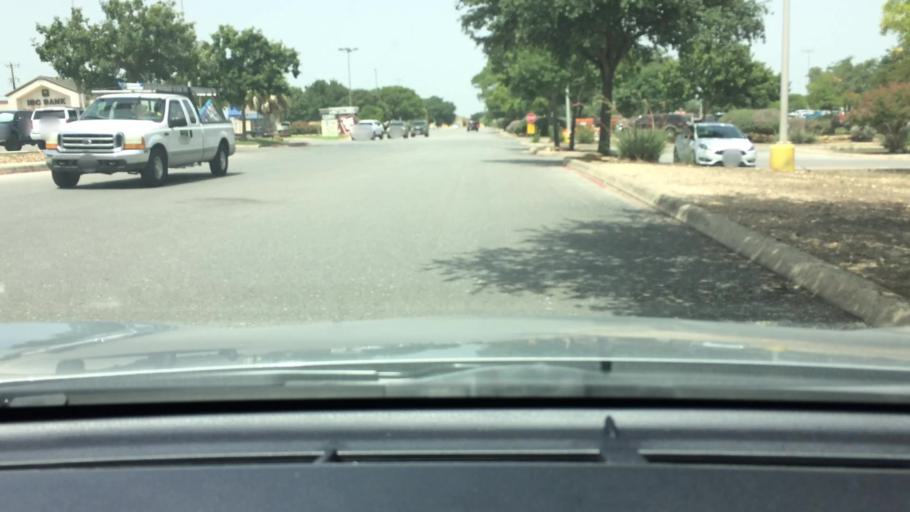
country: US
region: Texas
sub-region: Bexar County
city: San Antonio
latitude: 29.3527
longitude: -98.4397
